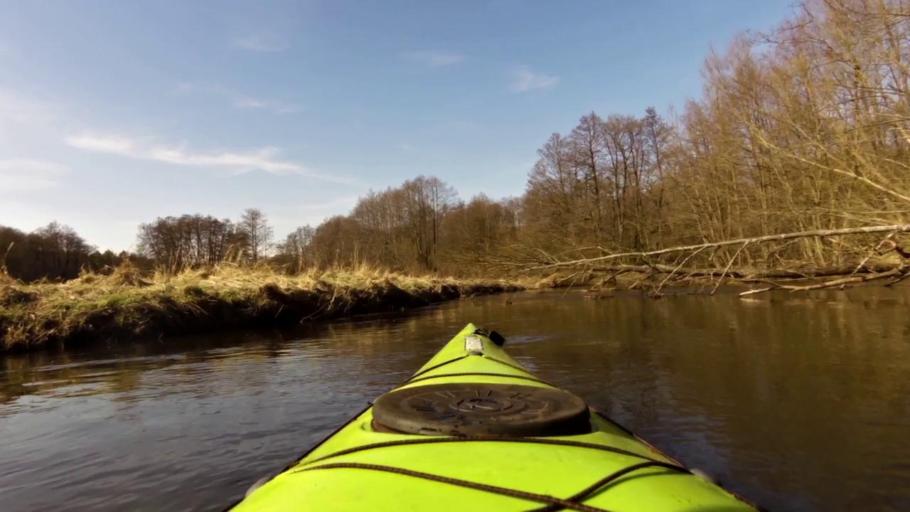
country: PL
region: West Pomeranian Voivodeship
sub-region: Powiat lobeski
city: Lobez
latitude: 53.7021
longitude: 15.5537
